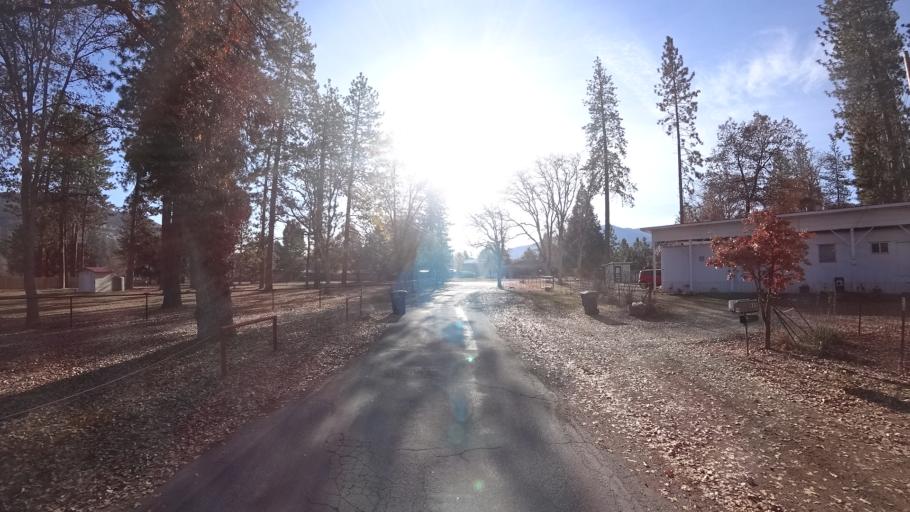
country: US
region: California
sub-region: Siskiyou County
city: Yreka
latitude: 41.6837
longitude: -122.6397
